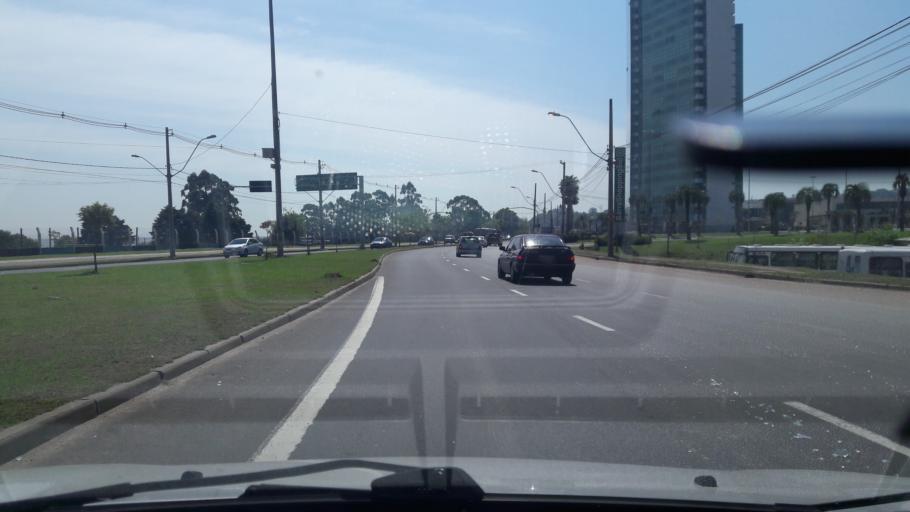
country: BR
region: Rio Grande do Sul
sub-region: Porto Alegre
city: Porto Alegre
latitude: -30.0886
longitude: -51.2481
